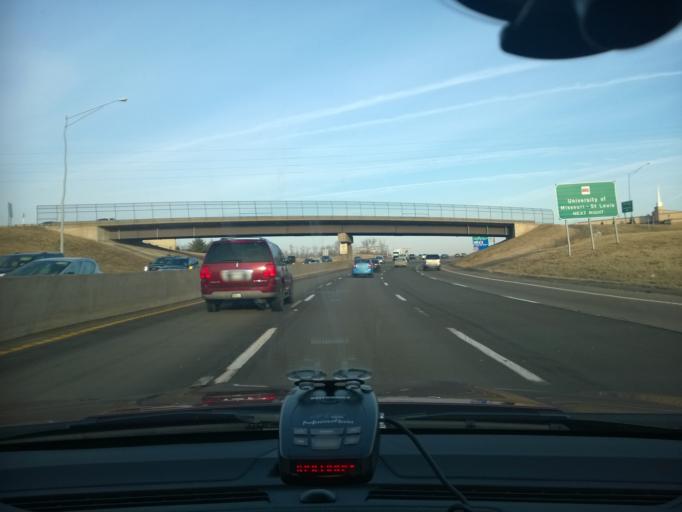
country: US
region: Missouri
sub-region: Saint Louis County
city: Normandy
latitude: 38.7164
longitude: -90.2967
